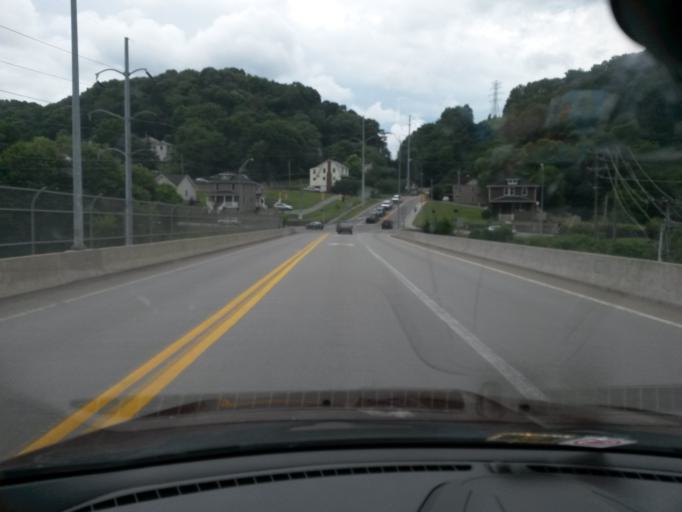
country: US
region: West Virginia
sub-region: Mercer County
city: Bluefield
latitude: 37.2634
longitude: -81.2384
